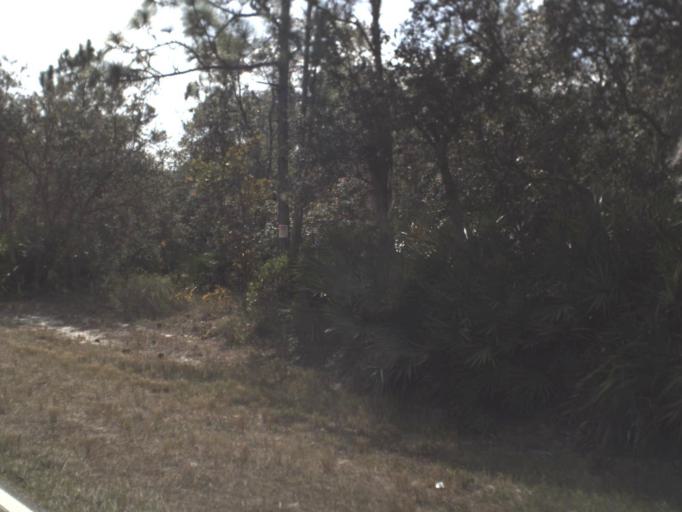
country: US
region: Florida
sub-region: Osceola County
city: Poinciana
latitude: 28.1925
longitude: -81.4675
